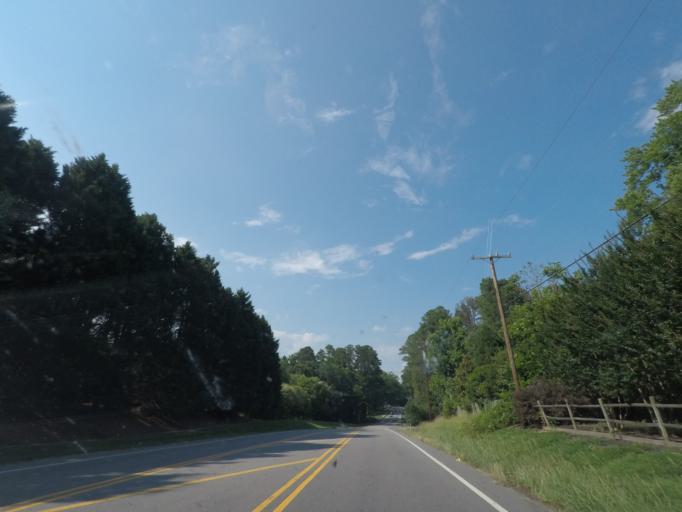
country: US
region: North Carolina
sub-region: Durham County
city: Durham
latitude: 35.9299
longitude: -78.9526
